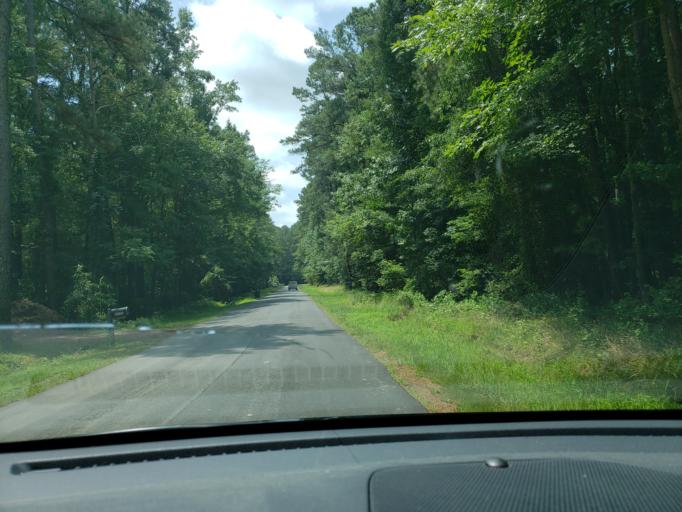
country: US
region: North Carolina
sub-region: Orange County
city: Chapel Hill
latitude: 35.9890
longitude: -78.9974
